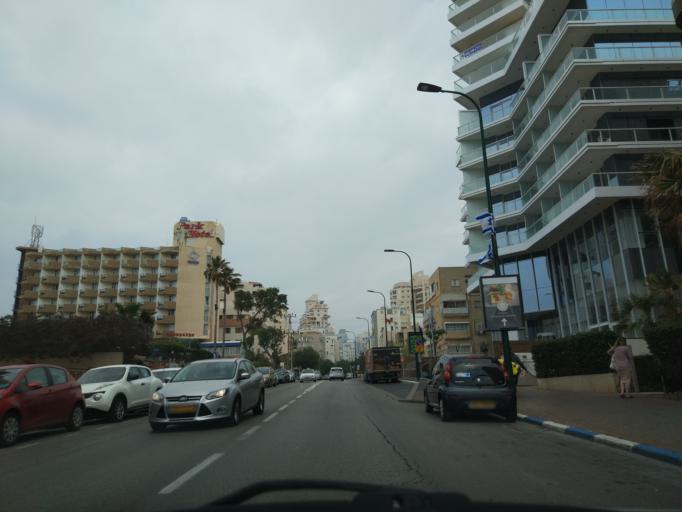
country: IL
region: Central District
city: Netanya
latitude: 32.3314
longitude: 34.8512
